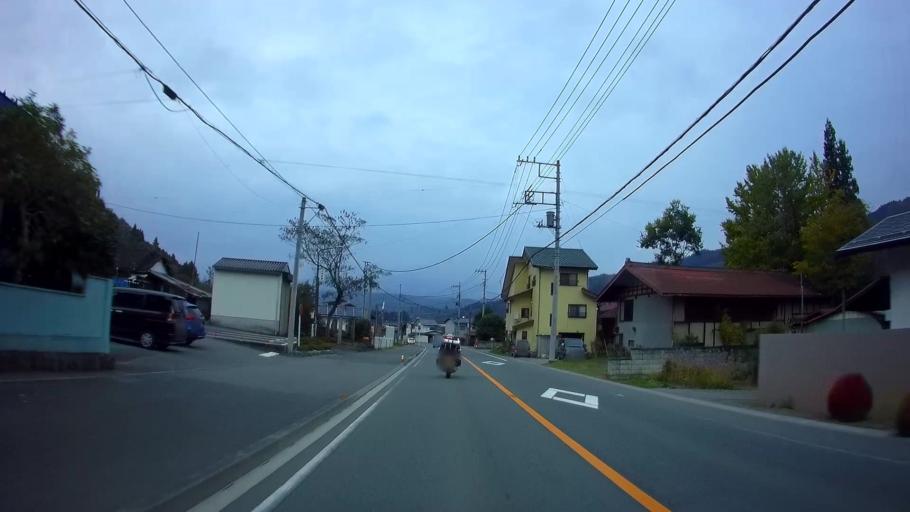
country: JP
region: Gunma
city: Nakanojomachi
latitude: 36.5589
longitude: 138.7691
